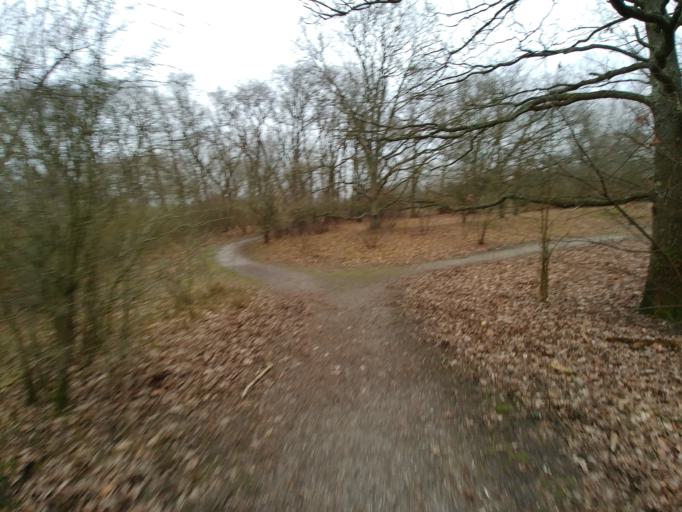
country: NL
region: South Holland
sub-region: Gemeente Den Haag
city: The Hague
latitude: 52.1125
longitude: 4.3266
